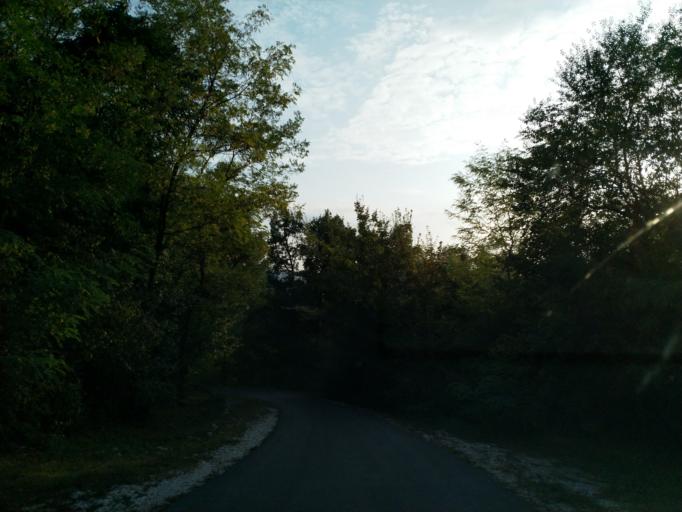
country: RS
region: Central Serbia
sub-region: Sumadijski Okrug
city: Arangelovac
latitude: 44.3140
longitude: 20.5915
